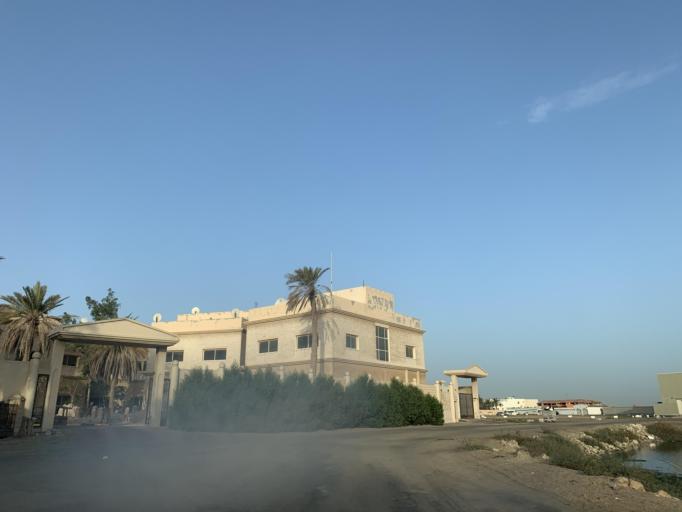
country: BH
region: Manama
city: Manama
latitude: 26.1866
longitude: 50.5853
